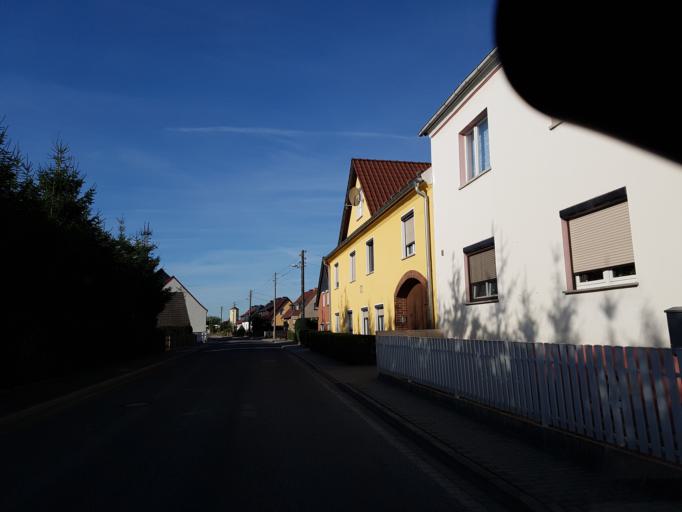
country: DE
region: Brandenburg
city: Elsterwerda
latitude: 51.4638
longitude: 13.4638
